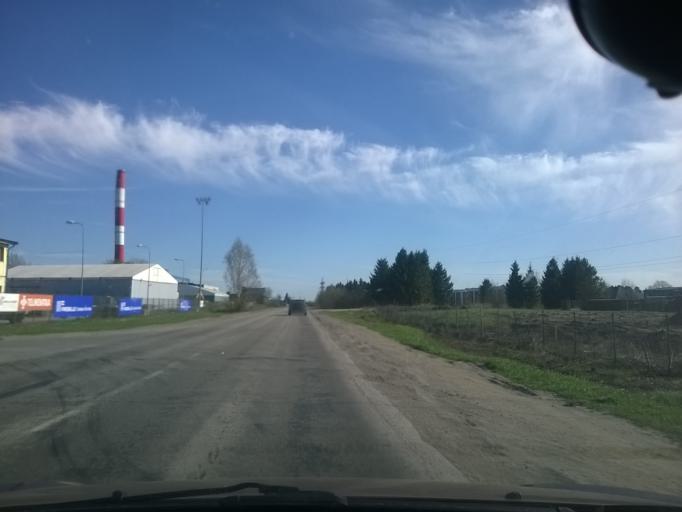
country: EE
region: Harju
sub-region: Joelaehtme vald
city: Loo
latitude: 59.4592
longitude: 24.9175
